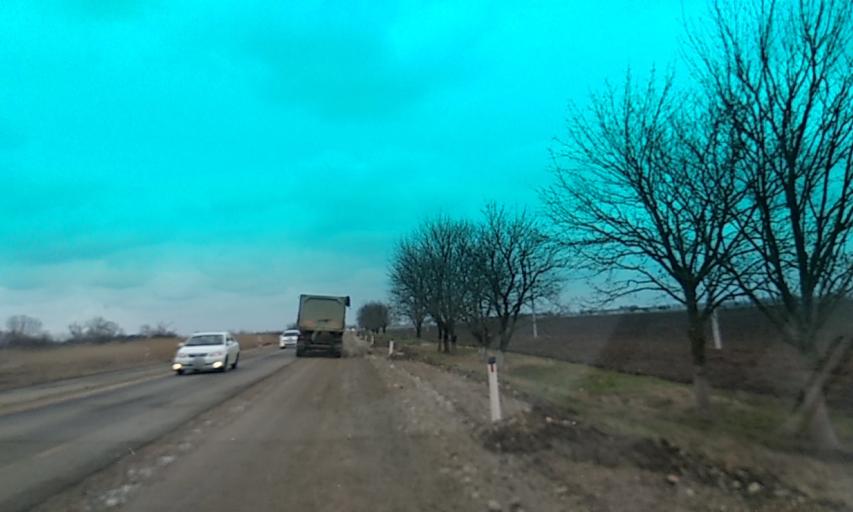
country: RU
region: Krasnodarskiy
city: Velikovechnoye
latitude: 44.9946
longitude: 39.7118
